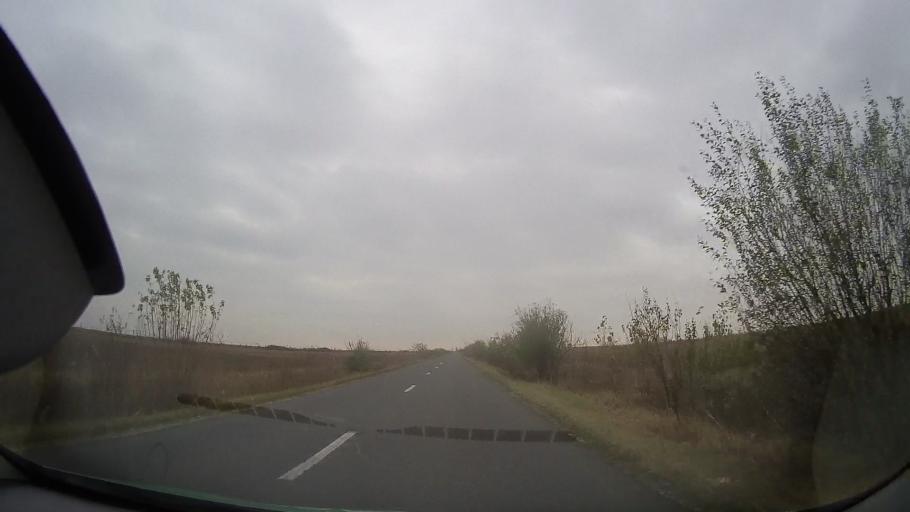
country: RO
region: Ialomita
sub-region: Comuna Manasia
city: Manasia
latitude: 44.7291
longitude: 26.6961
